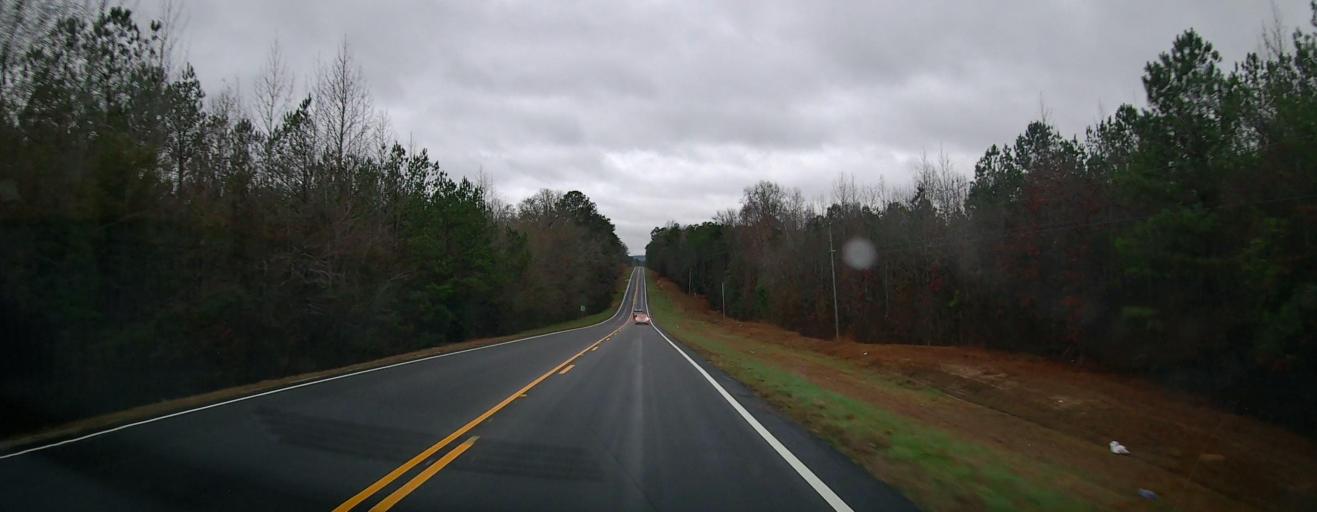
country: US
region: Alabama
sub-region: Bibb County
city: Centreville
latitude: 32.8216
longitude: -86.9424
